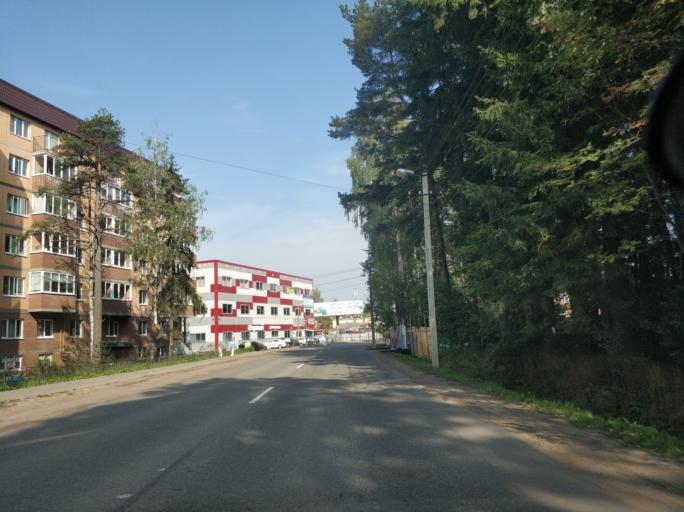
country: RU
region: Leningrad
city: Vsevolozhsk
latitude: 60.0164
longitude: 30.6236
